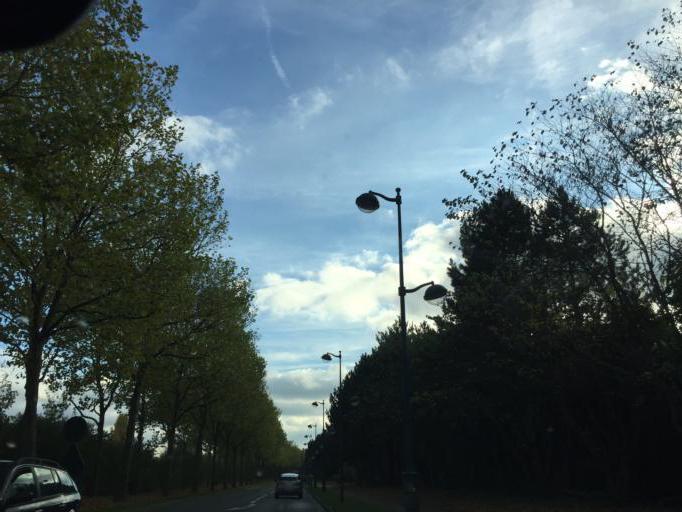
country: FR
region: Ile-de-France
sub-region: Departement de Seine-et-Marne
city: Serris
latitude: 48.8675
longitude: 2.7917
